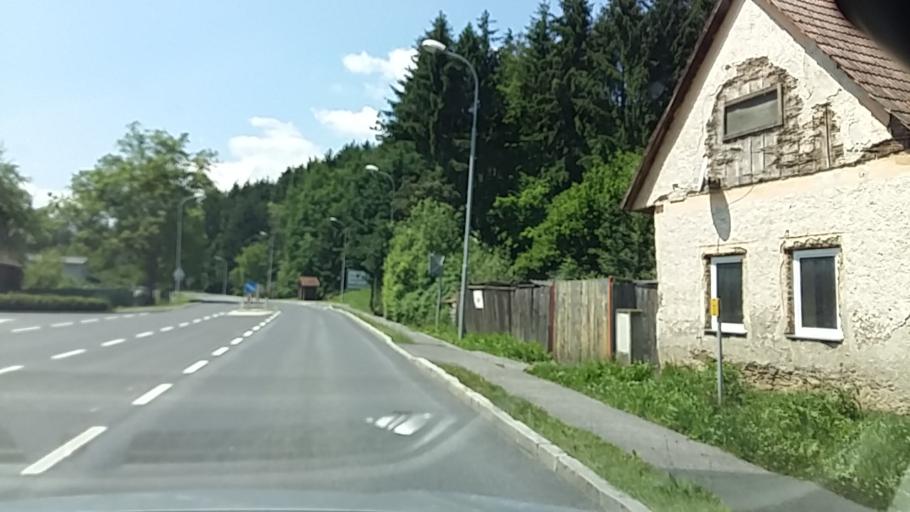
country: AT
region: Burgenland
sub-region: Politischer Bezirk Oberpullendorf
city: Lockenhaus
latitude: 47.4031
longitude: 16.3743
